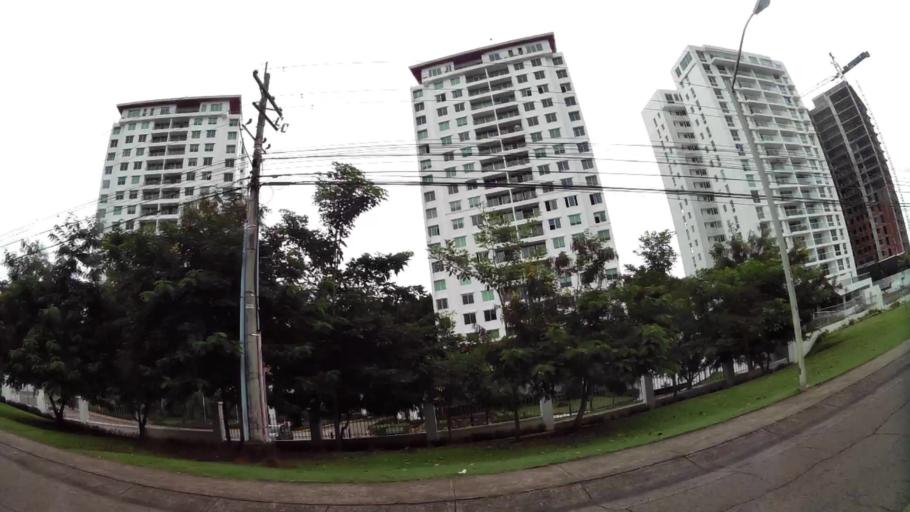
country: PA
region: Panama
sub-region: Distrito de Panama
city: Ancon
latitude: 9.0055
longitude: -79.5695
